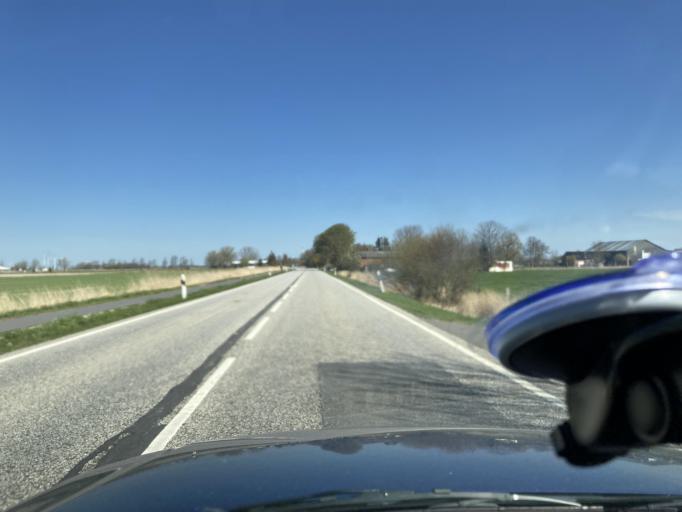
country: DE
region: Schleswig-Holstein
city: Epenwohrden
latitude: 54.1062
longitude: 9.0595
